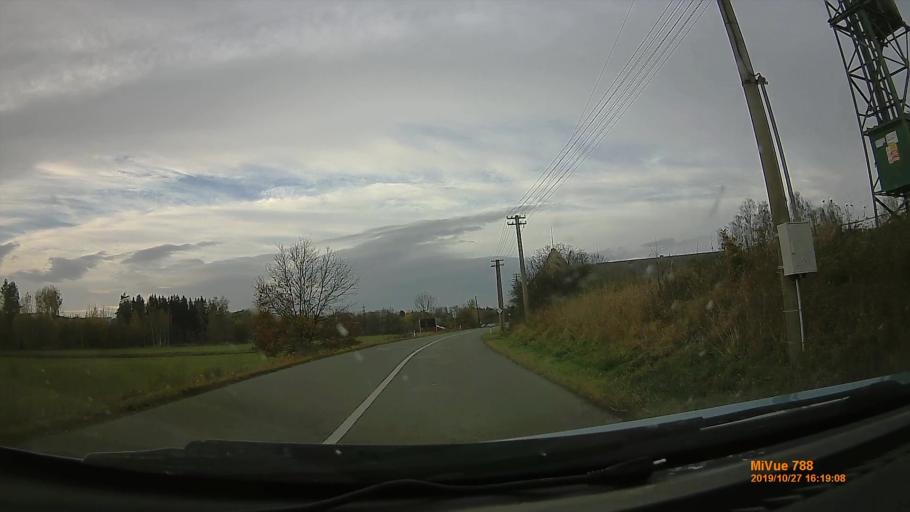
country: CZ
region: Kralovehradecky
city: Broumov
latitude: 50.5706
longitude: 16.3465
